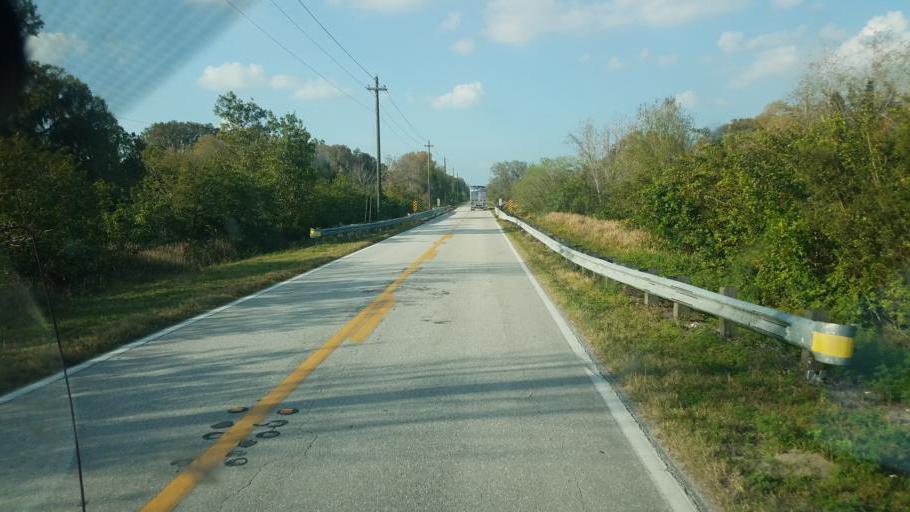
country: US
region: Florida
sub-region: Hardee County
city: Bowling Green
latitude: 27.6901
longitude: -81.9563
